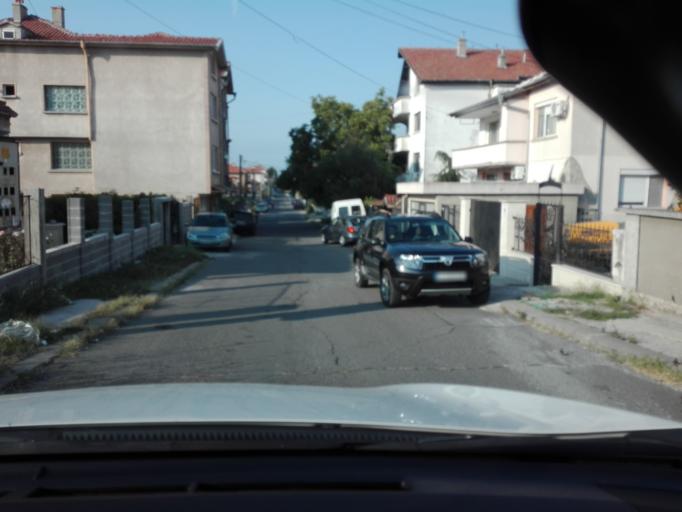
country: BG
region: Burgas
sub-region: Obshtina Burgas
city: Burgas
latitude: 42.4598
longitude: 27.4094
